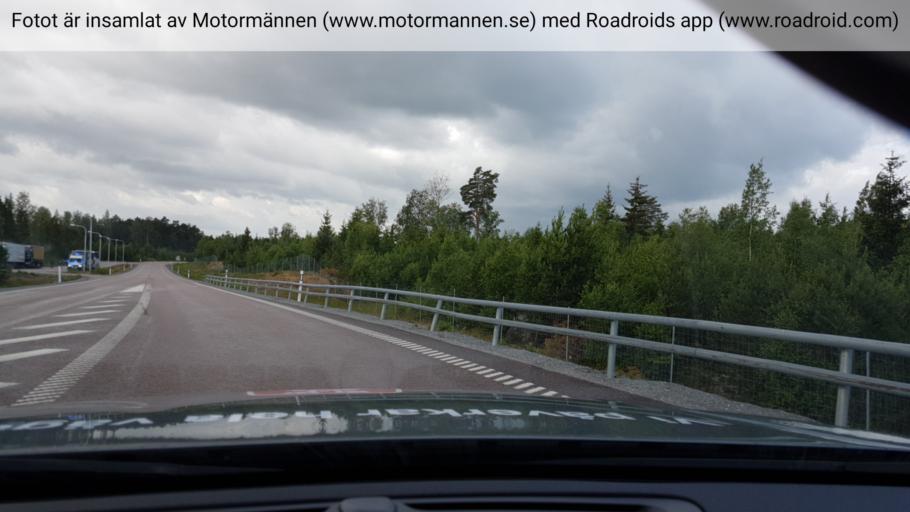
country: SE
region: Uppsala
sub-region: Enkopings Kommun
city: Hummelsta
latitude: 59.6407
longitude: 16.8824
